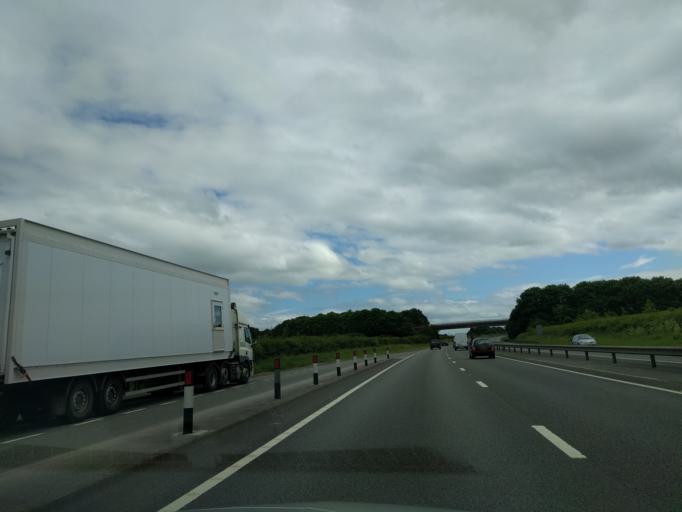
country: GB
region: England
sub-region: Nottinghamshire
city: Newark on Trent
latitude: 53.0658
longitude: -0.7654
